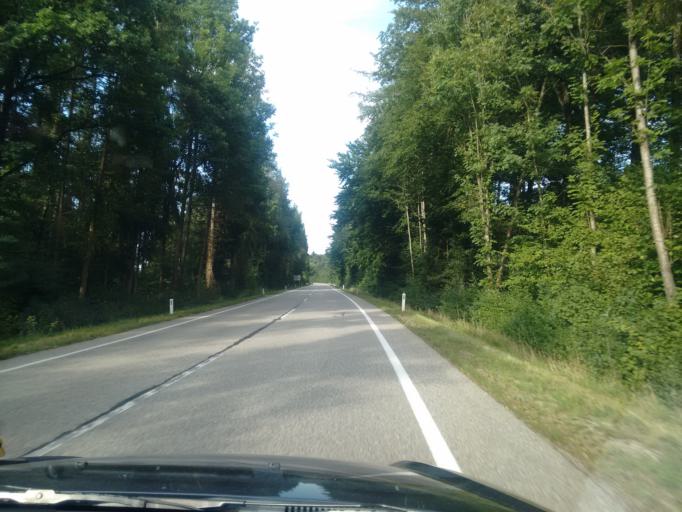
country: DE
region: Bavaria
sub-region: Upper Bavaria
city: Haiming
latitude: 48.1897
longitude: 12.8908
